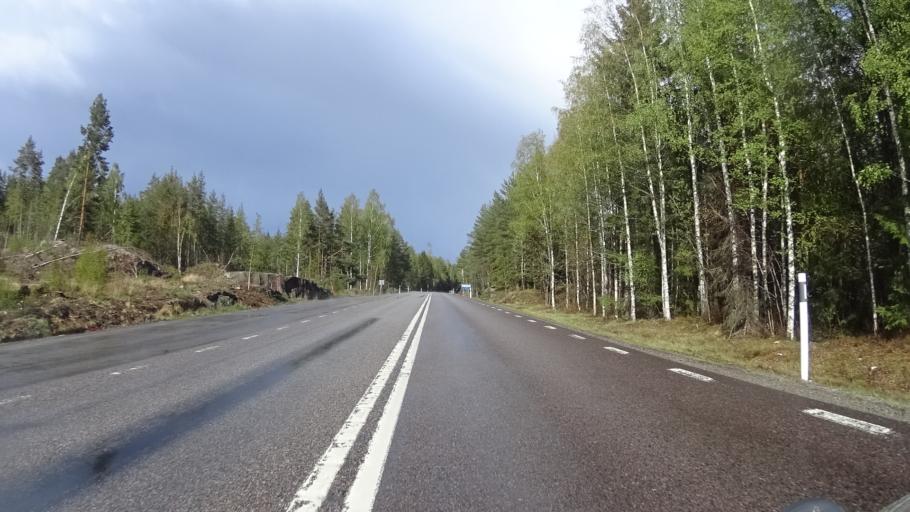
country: SE
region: OErebro
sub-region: Askersunds Kommun
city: Askersund
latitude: 58.7136
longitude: 14.7359
